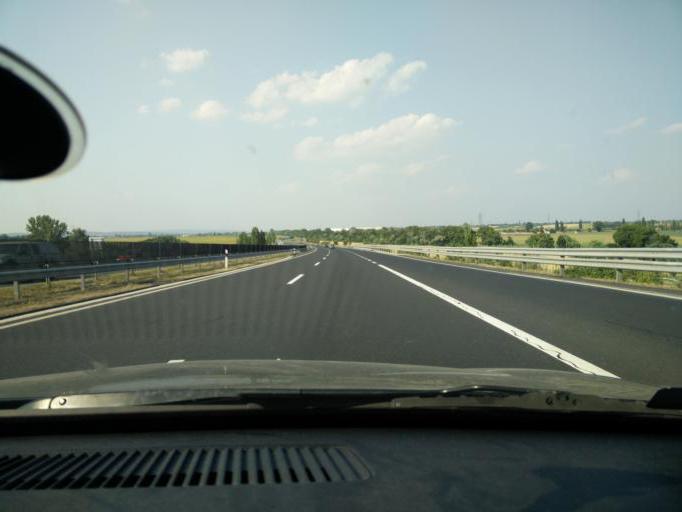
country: HU
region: Pest
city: Szazhalombatta
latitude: 47.3389
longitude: 18.8951
